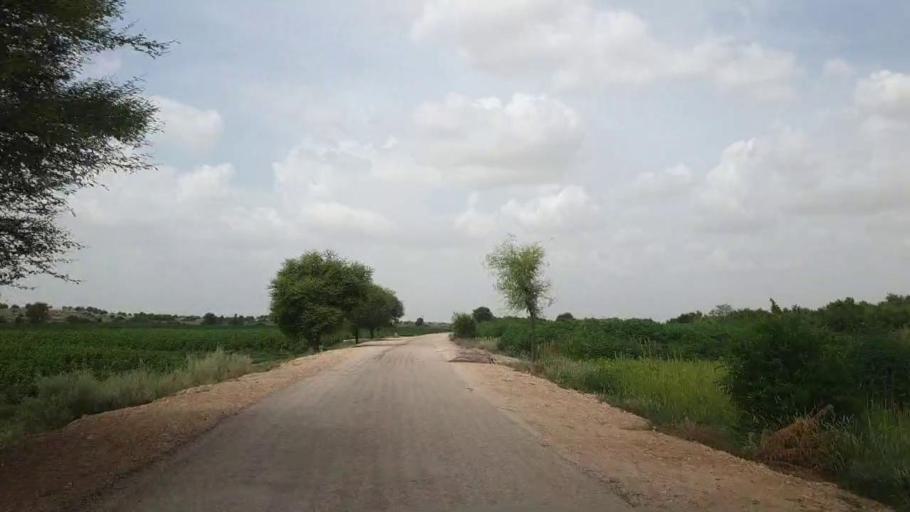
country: PK
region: Sindh
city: Kot Diji
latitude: 27.2215
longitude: 69.0843
